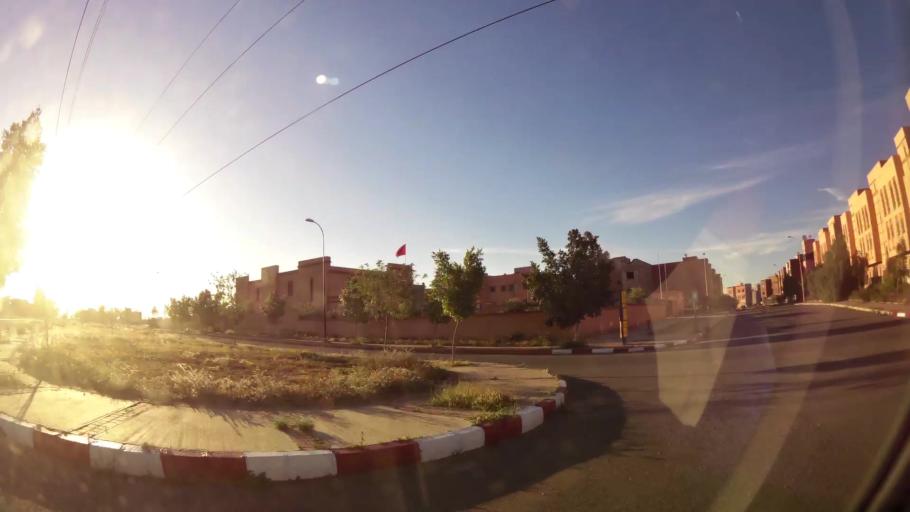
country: MA
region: Marrakech-Tensift-Al Haouz
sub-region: Marrakech
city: Marrakesh
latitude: 31.7428
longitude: -8.1167
